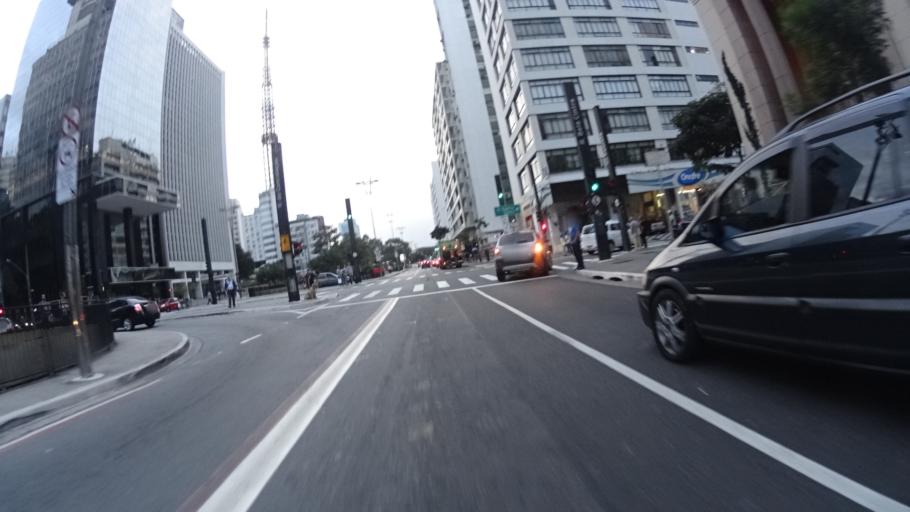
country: BR
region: Sao Paulo
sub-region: Sao Paulo
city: Sao Paulo
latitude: -23.5567
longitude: -46.6616
